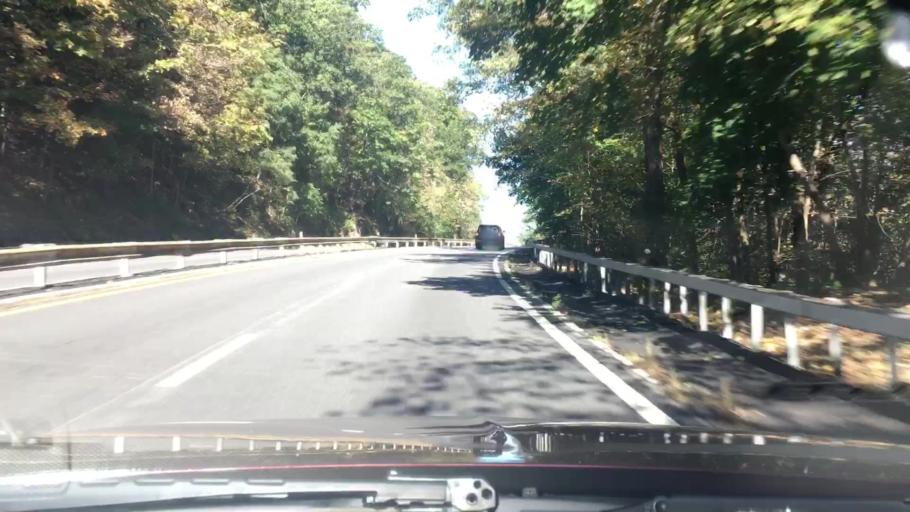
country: US
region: New York
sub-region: Westchester County
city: Chappaqua
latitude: 41.1627
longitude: -73.7724
